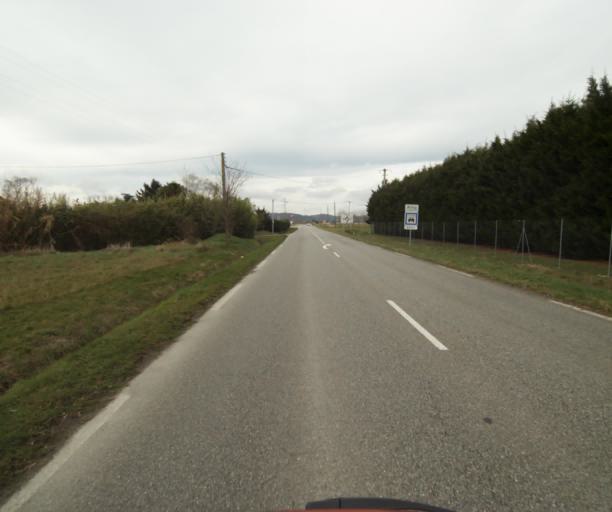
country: FR
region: Midi-Pyrenees
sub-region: Departement de l'Ariege
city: La Tour-du-Crieu
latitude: 43.0970
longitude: 1.6577
